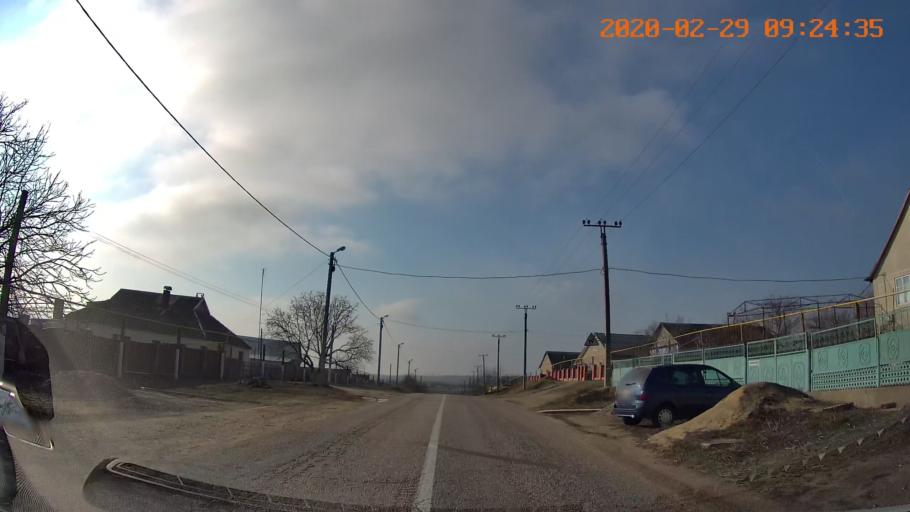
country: MD
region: Telenesti
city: Pervomaisc
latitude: 46.7148
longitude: 29.9582
